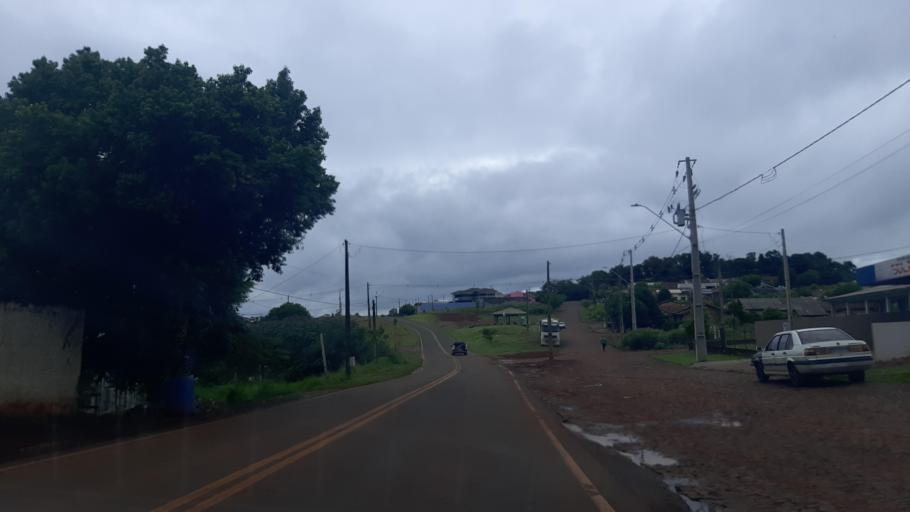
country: BR
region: Parana
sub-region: Ampere
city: Ampere
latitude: -25.9285
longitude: -53.4667
